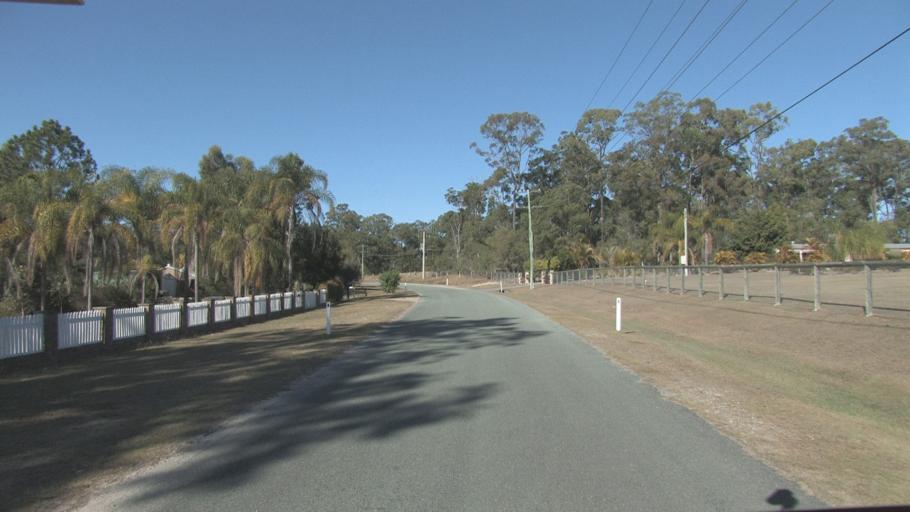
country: AU
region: Queensland
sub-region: Logan
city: Chambers Flat
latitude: -27.7904
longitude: 153.1317
